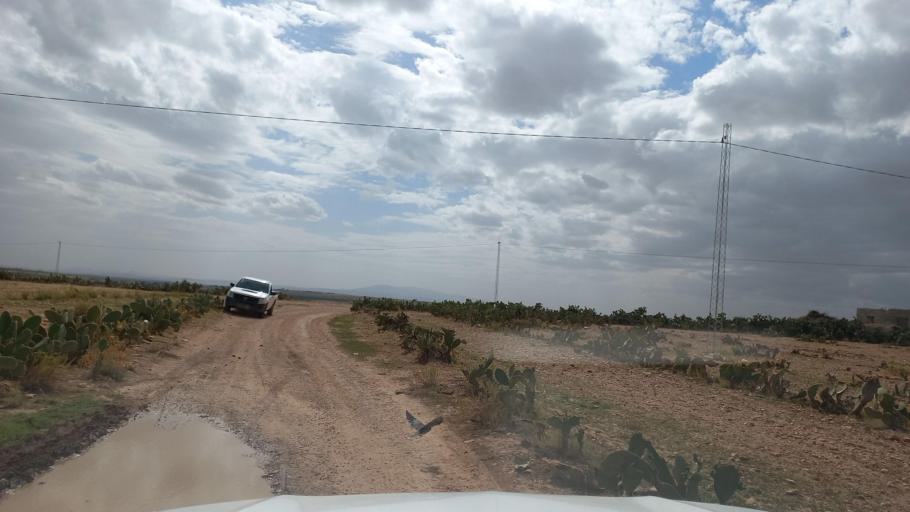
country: TN
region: Al Qasrayn
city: Sbiba
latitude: 35.3818
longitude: 9.0942
